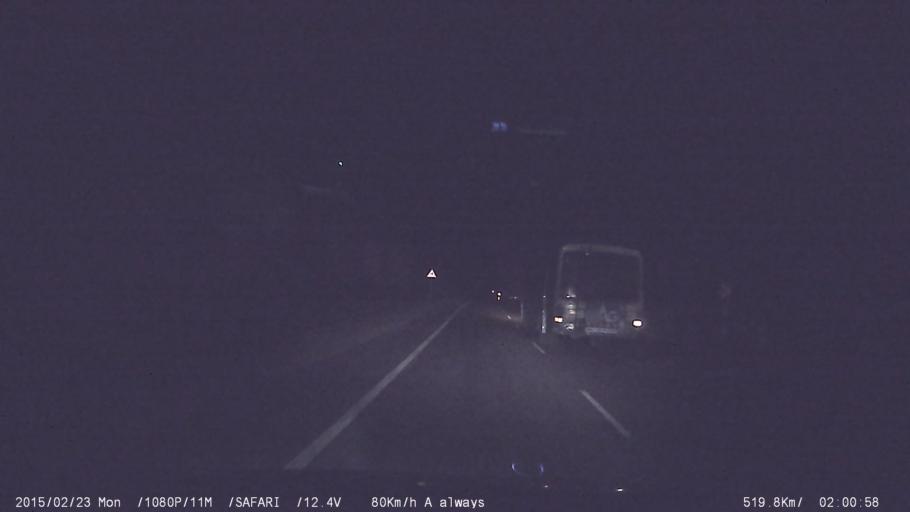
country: IN
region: Tamil Nadu
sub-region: Krishnagiri
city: Krishnagiri
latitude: 12.6280
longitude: 78.0778
